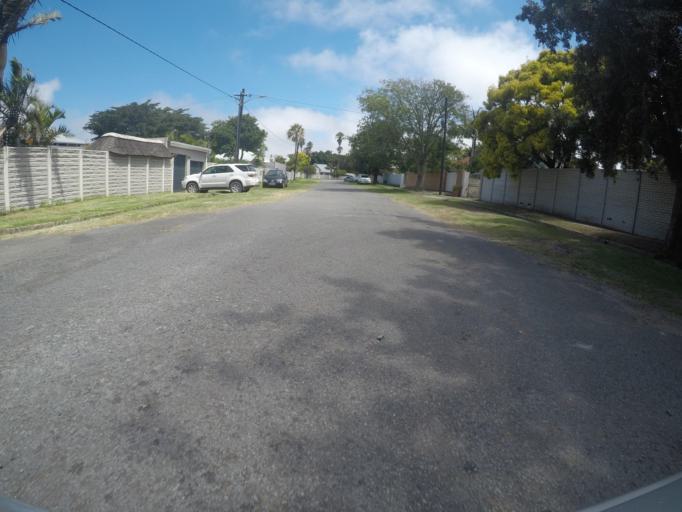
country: ZA
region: Eastern Cape
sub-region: Buffalo City Metropolitan Municipality
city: East London
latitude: -32.9740
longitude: 27.9009
